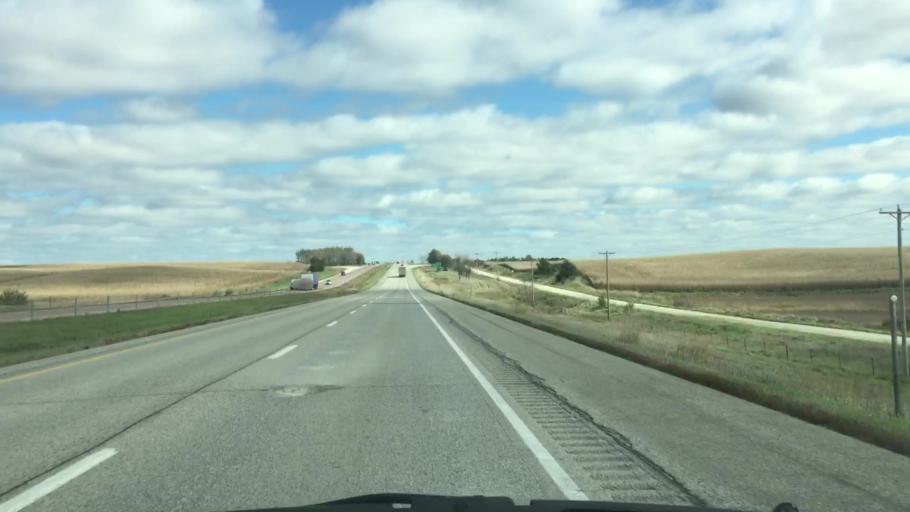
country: US
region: Iowa
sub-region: Iowa County
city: Marengo
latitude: 41.6960
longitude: -92.1748
